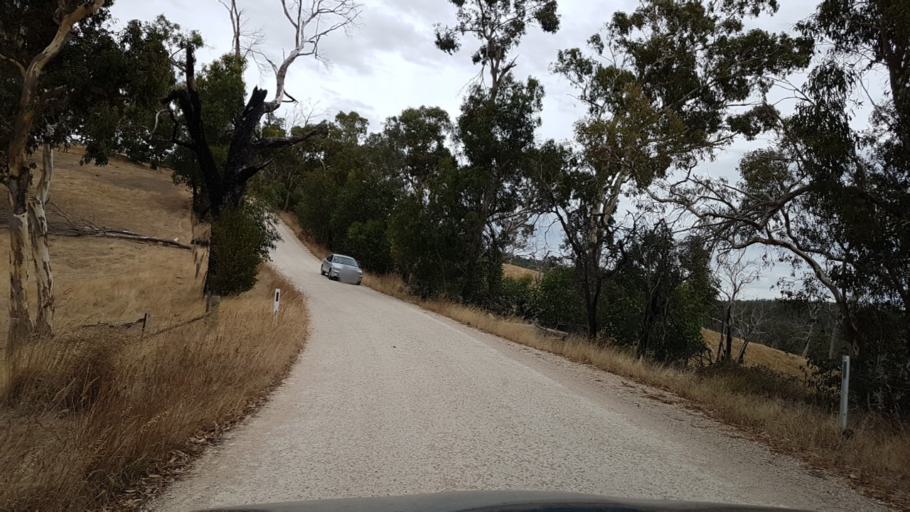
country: AU
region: South Australia
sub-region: Adelaide Hills
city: Gumeracha
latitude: -34.7974
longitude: 138.8178
